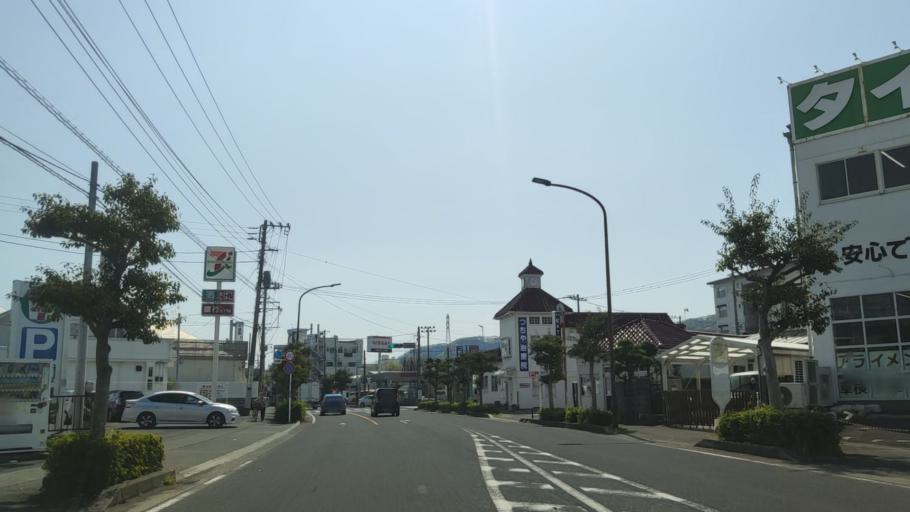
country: JP
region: Kanagawa
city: Oiso
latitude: 35.3367
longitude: 139.3065
